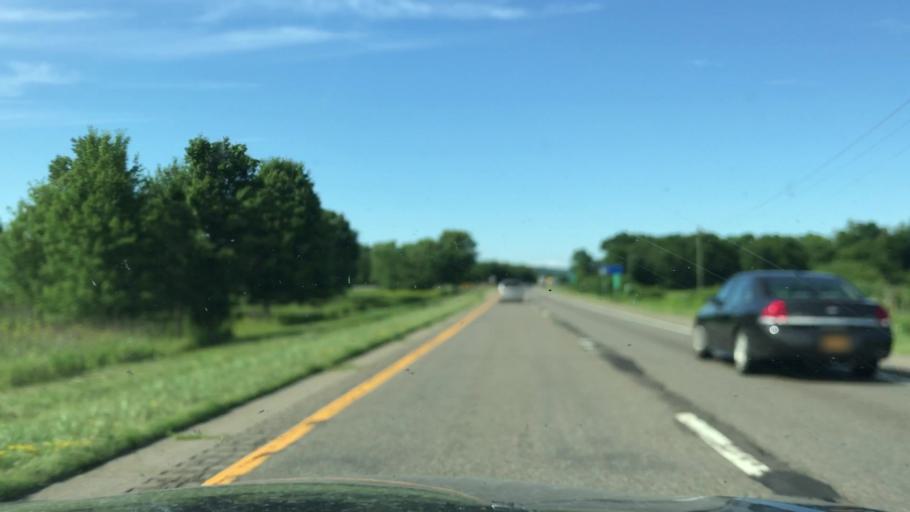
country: US
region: New York
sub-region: Tioga County
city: Owego
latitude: 42.0566
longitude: -76.3310
